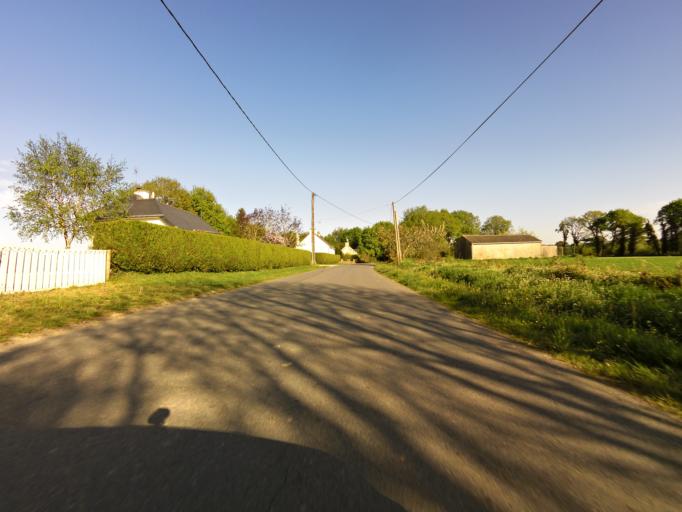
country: FR
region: Brittany
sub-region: Departement du Morbihan
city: Molac
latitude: 47.7422
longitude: -2.4578
